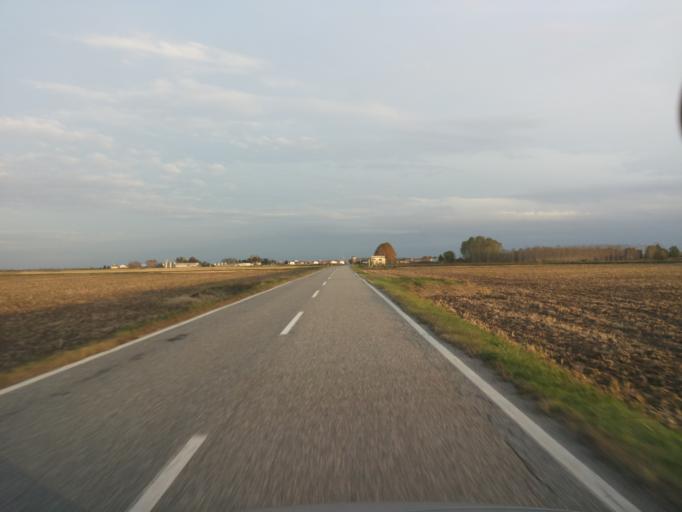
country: IT
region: Piedmont
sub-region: Provincia di Vercelli
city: Tricerro
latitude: 45.2424
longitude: 8.3473
